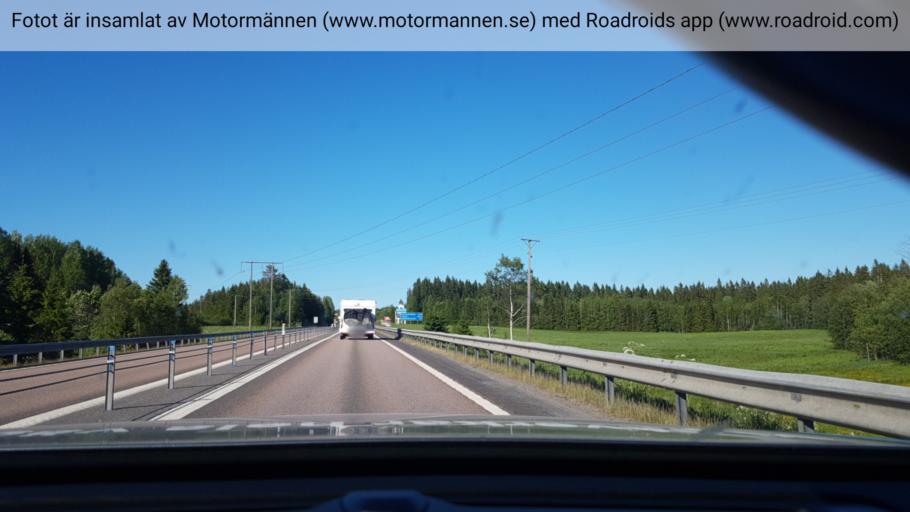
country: SE
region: Vaesternorrland
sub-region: Haernoesands Kommun
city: Haernoesand
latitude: 62.5910
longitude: 17.7936
